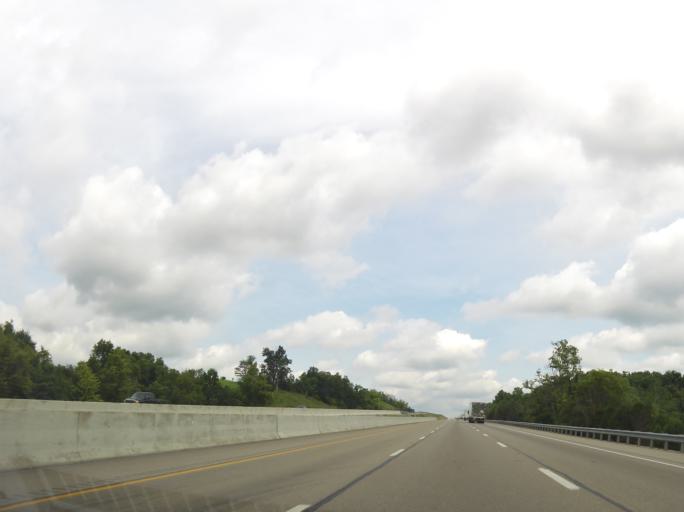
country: US
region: Kentucky
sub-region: Grant County
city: Williamstown
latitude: 38.5125
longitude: -84.5886
